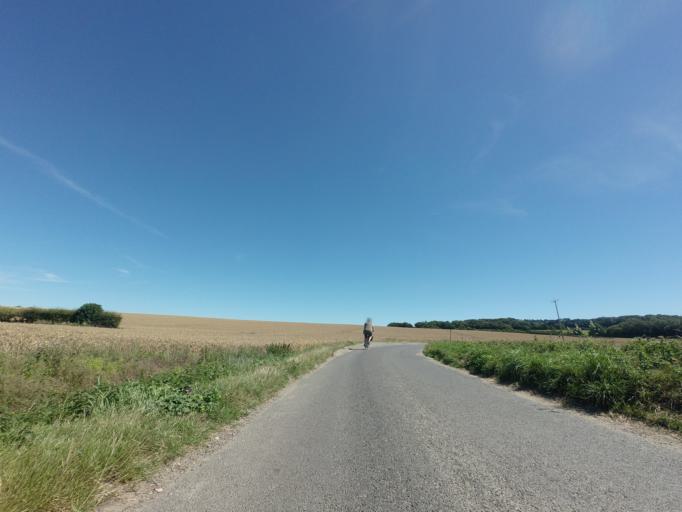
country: GB
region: England
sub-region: Kent
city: Deal
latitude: 51.1934
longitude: 1.3648
